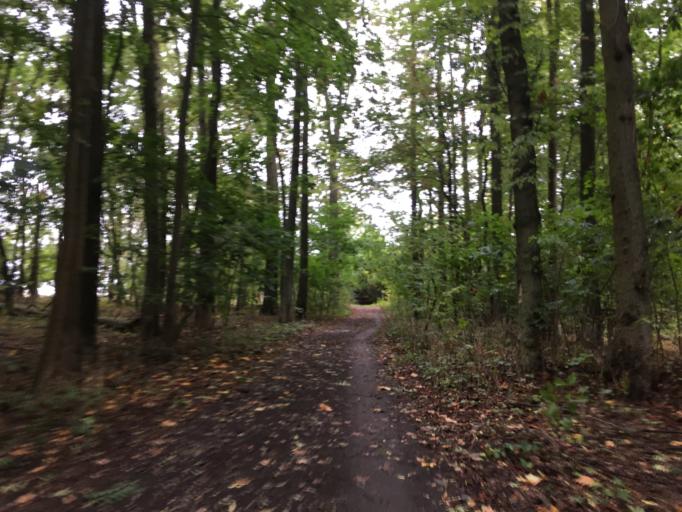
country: DE
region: Brandenburg
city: Ahrensfelde
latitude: 52.5951
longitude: 13.5891
